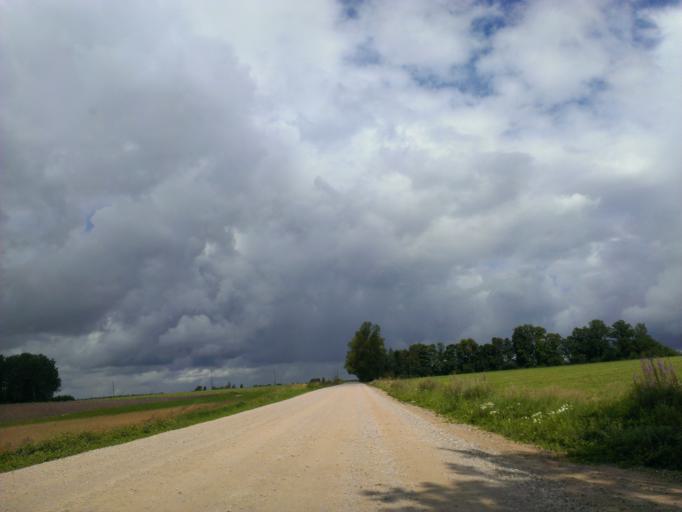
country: LV
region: Sigulda
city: Sigulda
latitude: 57.1752
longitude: 24.9228
